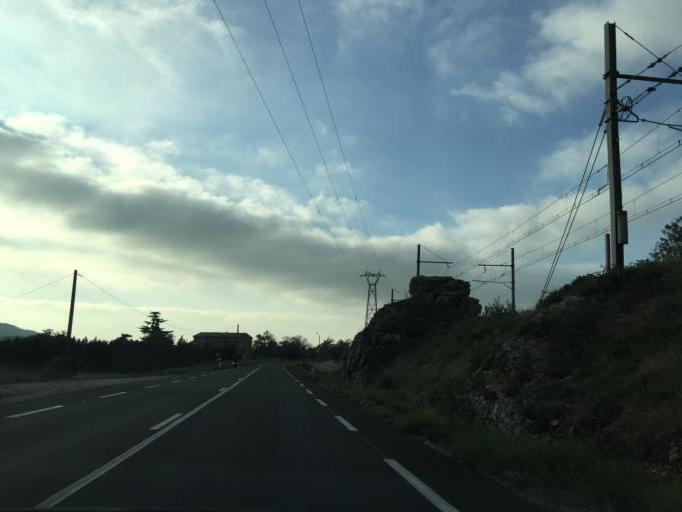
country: FR
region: Rhone-Alpes
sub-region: Departement de l'Ardeche
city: Viviers
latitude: 44.4647
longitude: 4.6886
